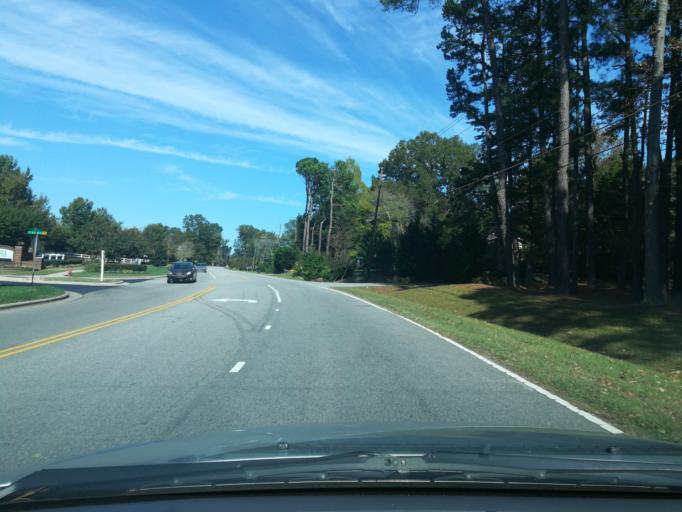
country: US
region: North Carolina
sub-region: Durham County
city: Durham
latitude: 35.9655
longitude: -78.9762
